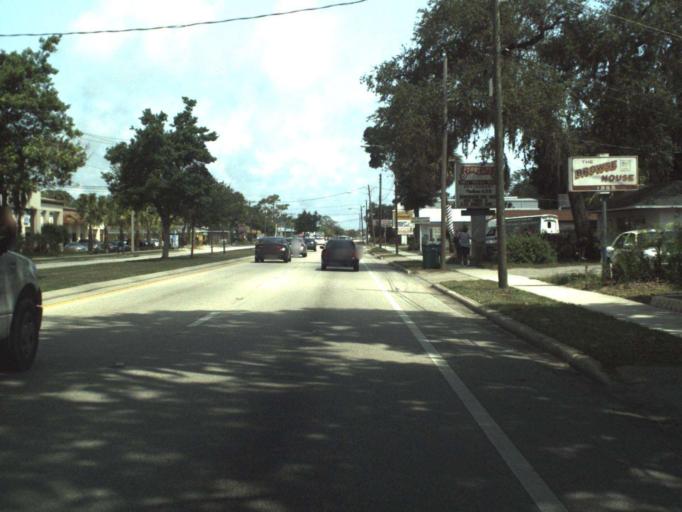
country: US
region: Florida
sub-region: Volusia County
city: Holly Hill
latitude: 29.2500
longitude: -81.0438
